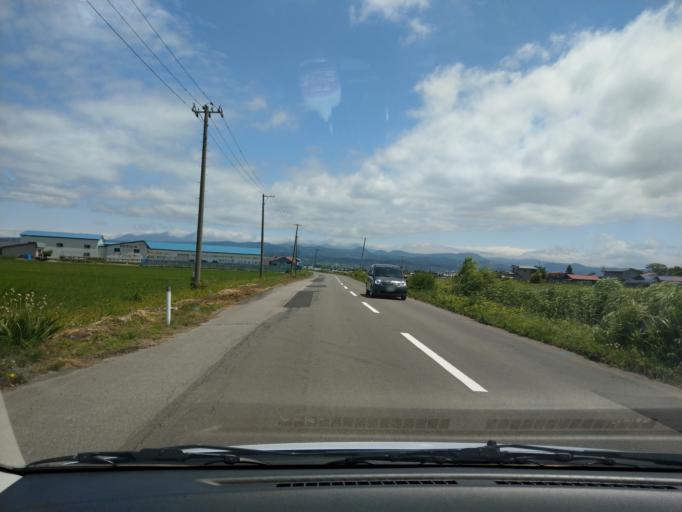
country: JP
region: Aomori
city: Namioka
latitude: 40.6839
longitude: 140.5574
